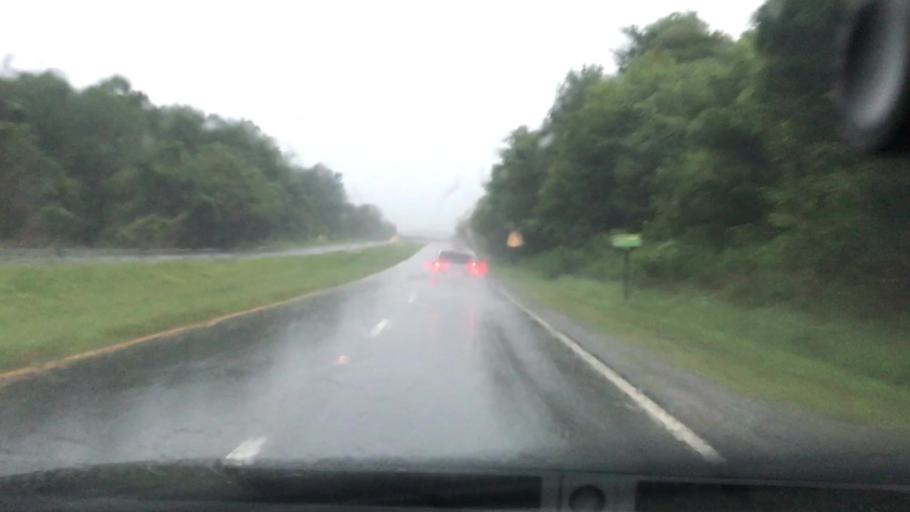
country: US
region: Virginia
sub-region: Giles County
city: Pearisburg
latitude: 37.3368
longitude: -80.7332
